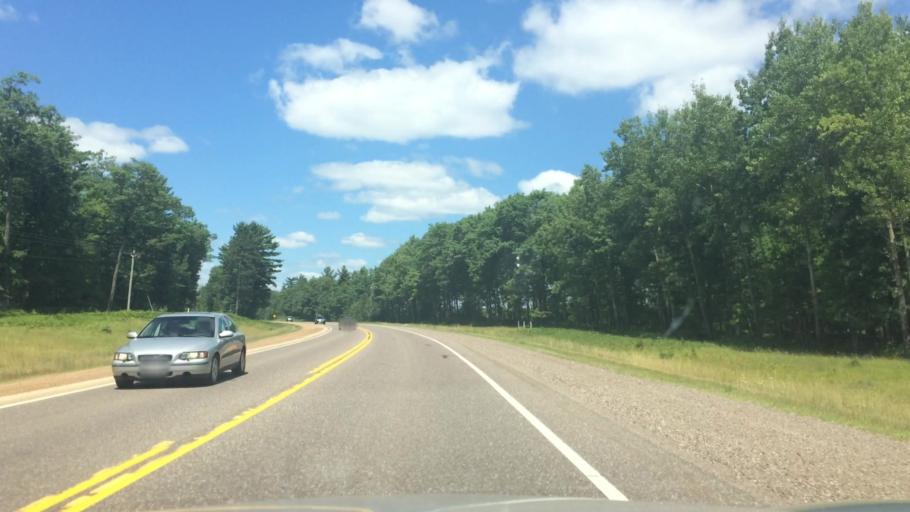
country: US
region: Wisconsin
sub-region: Vilas County
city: Lac du Flambeau
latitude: 45.9415
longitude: -89.6965
